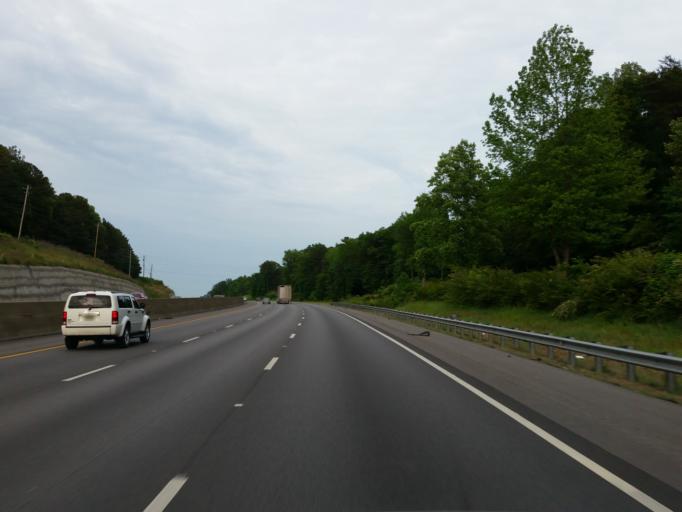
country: US
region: Alabama
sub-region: Saint Clair County
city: Pell City
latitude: 33.5946
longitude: -86.3521
